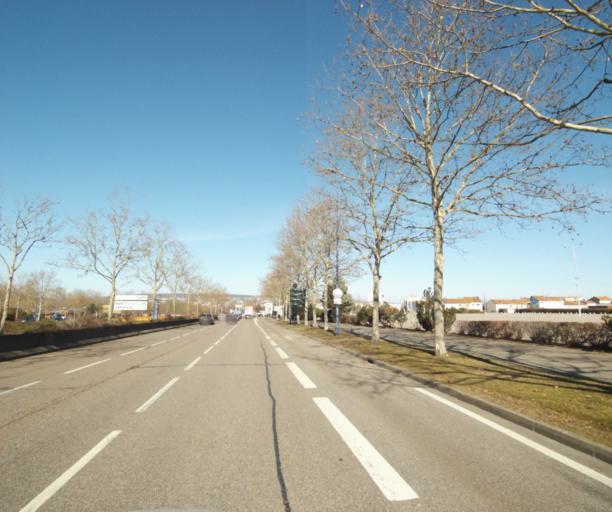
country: FR
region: Lorraine
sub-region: Departement de Meurthe-et-Moselle
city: Jarville-la-Malgrange
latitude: 48.6657
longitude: 6.1905
